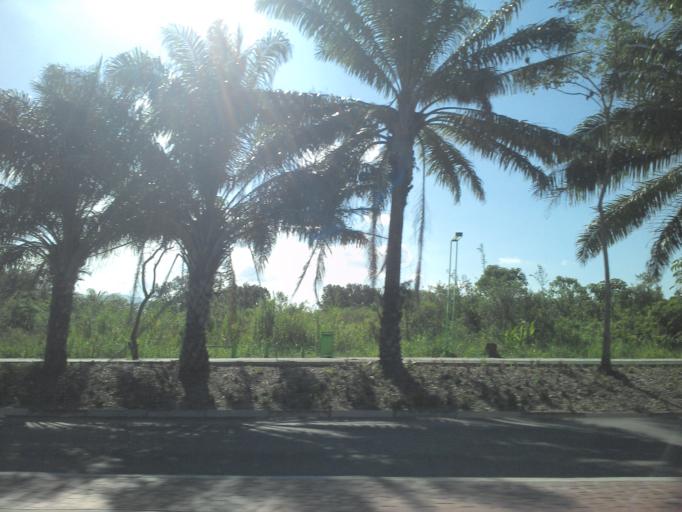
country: MX
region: Chiapas
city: Palenque
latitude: 17.5298
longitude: -91.9920
